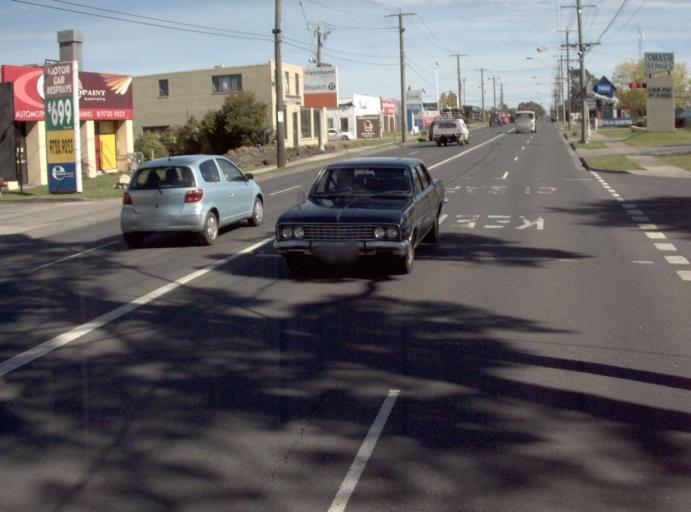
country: AU
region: Victoria
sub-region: Knox
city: Bayswater
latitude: -37.8404
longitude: 145.2708
